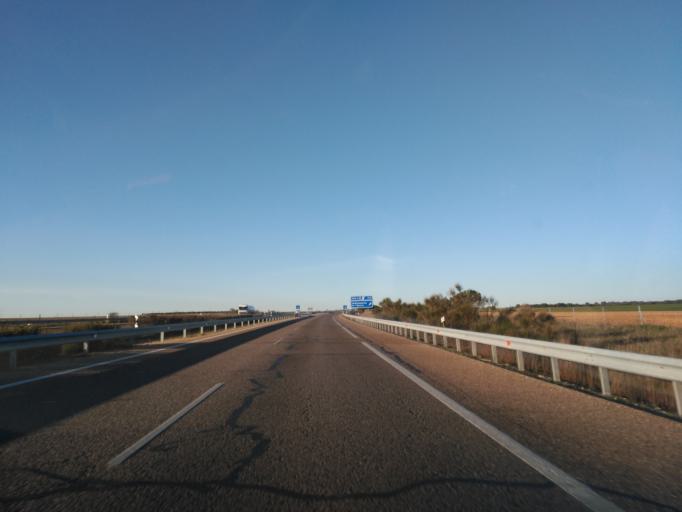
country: ES
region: Castille and Leon
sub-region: Provincia de Salamanca
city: Aldeanueva de Figueroa
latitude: 41.1257
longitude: -5.4899
